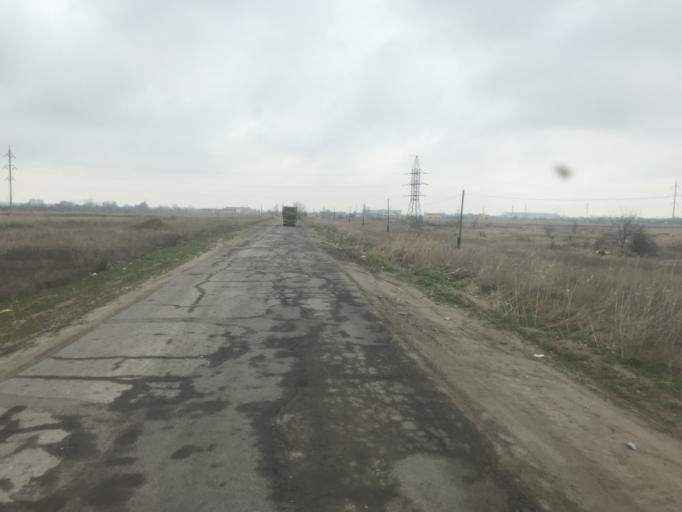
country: RU
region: Volgograd
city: Svetlyy Yar
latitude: 48.5171
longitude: 44.6291
